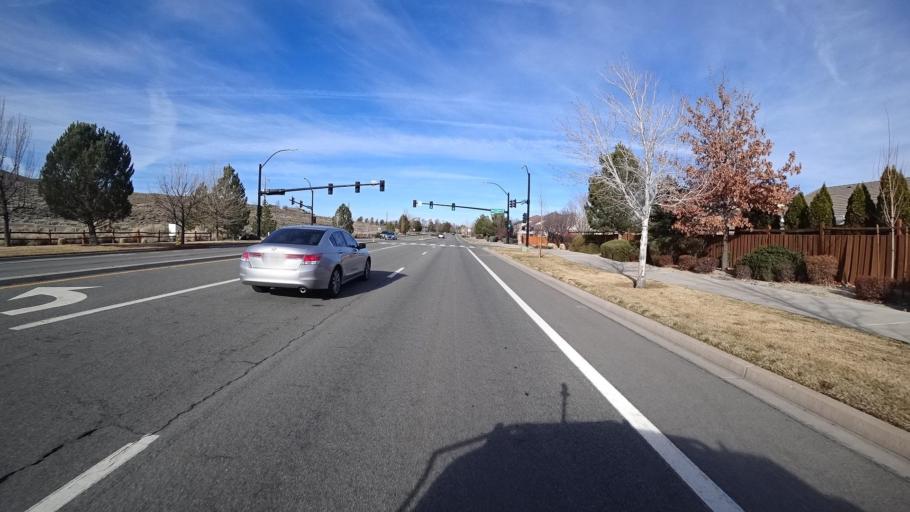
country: US
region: Nevada
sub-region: Washoe County
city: Spanish Springs
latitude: 39.6085
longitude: -119.6735
